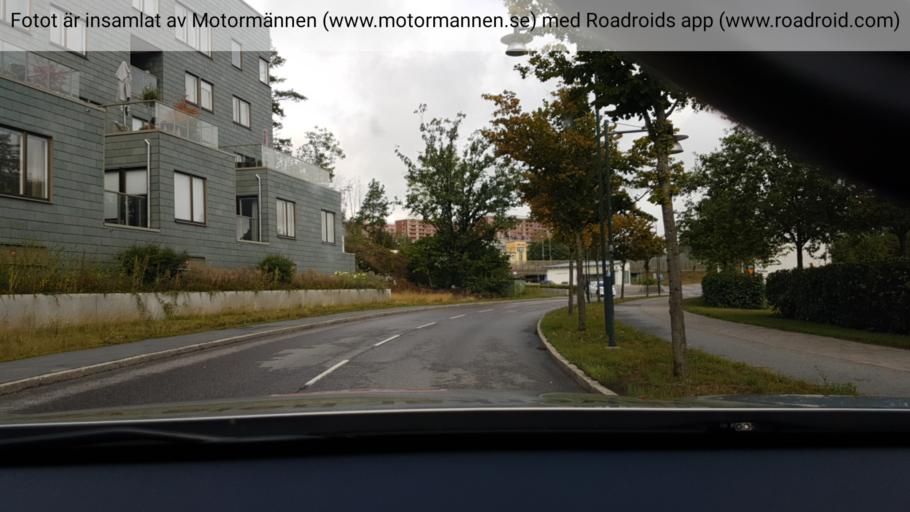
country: SE
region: Stockholm
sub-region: Norrtalje Kommun
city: Bergshamra
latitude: 59.3840
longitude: 18.0463
